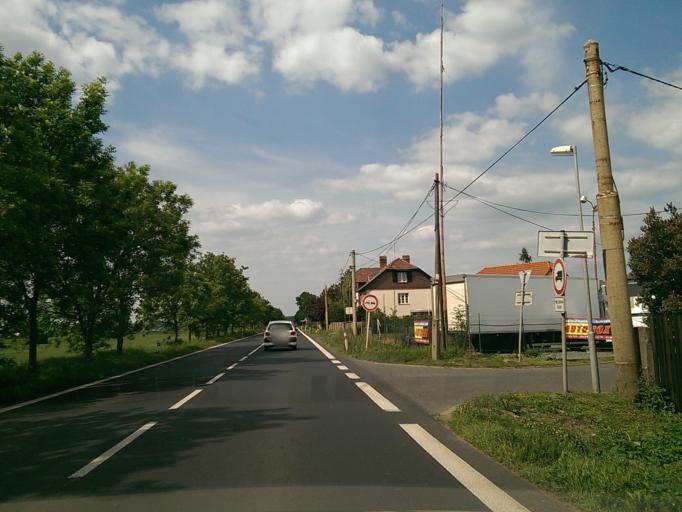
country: CZ
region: Central Bohemia
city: Libis
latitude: 50.2732
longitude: 14.4959
